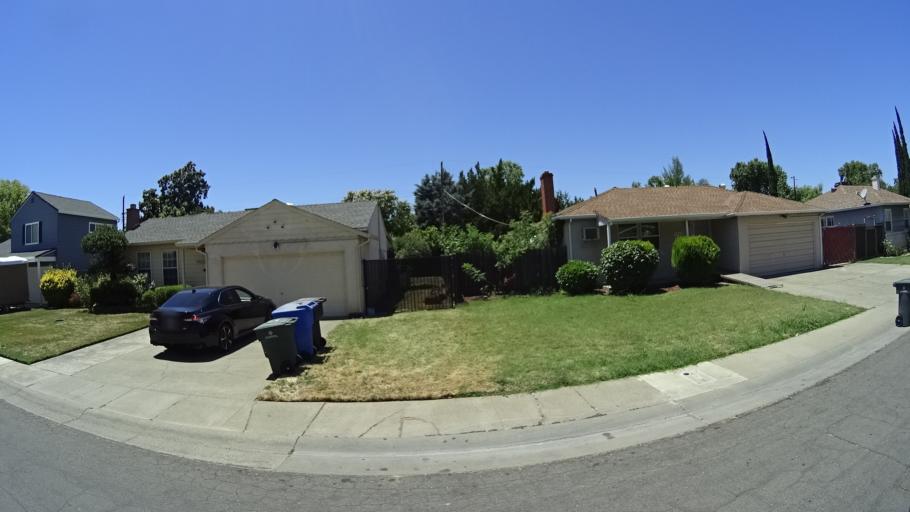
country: US
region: California
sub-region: Sacramento County
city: Parkway
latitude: 38.5296
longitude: -121.4906
